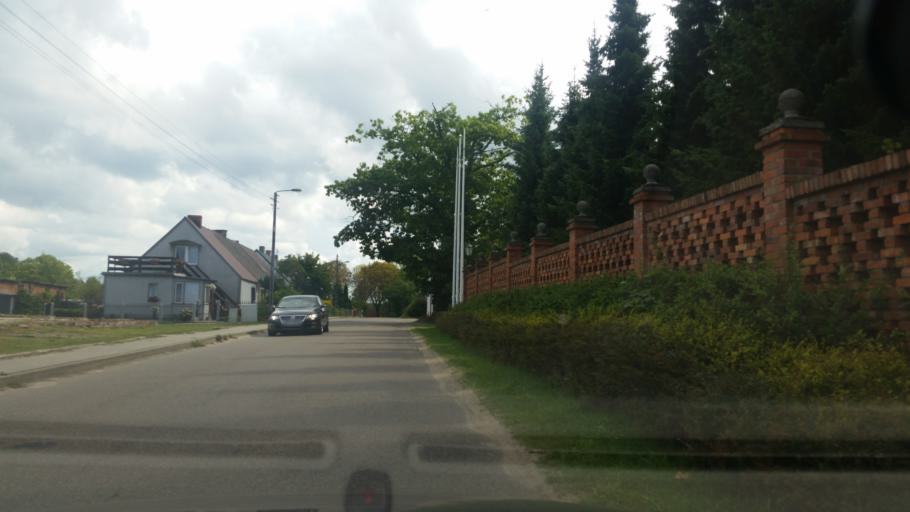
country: PL
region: Pomeranian Voivodeship
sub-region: Powiat wejherowski
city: Choczewo
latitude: 54.7470
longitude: 17.7974
